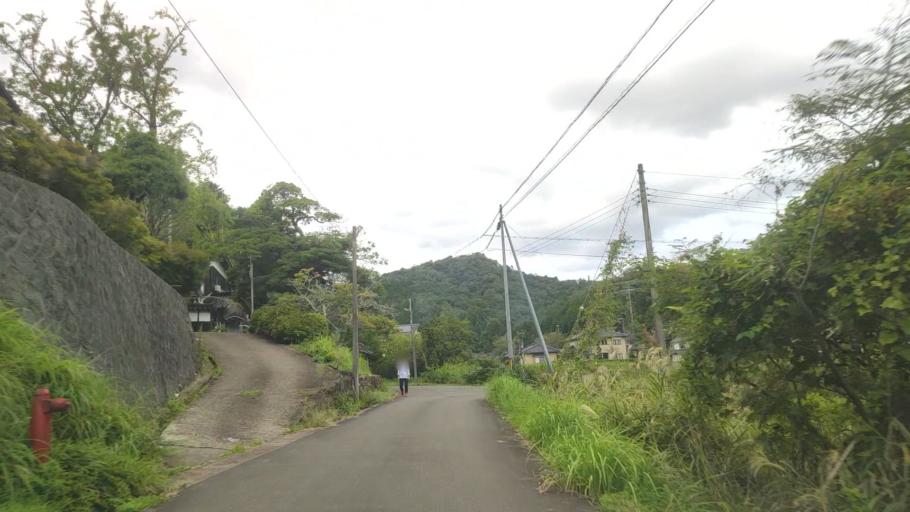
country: JP
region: Hyogo
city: Toyooka
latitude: 35.5985
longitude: 134.8820
